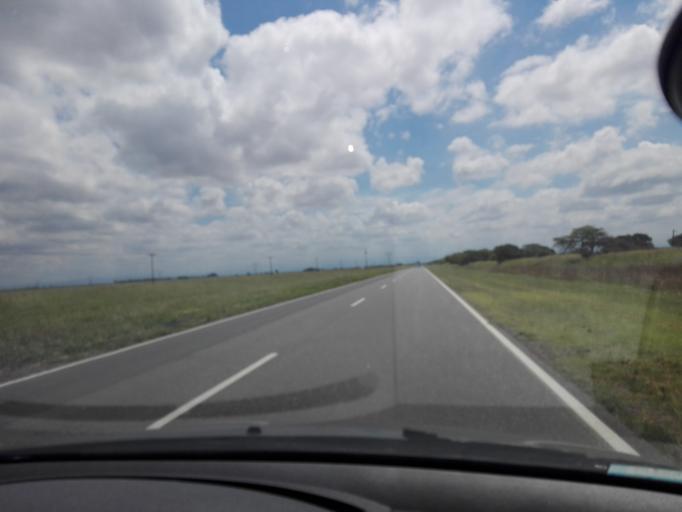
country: AR
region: Cordoba
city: Toledo
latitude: -31.6456
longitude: -64.0272
